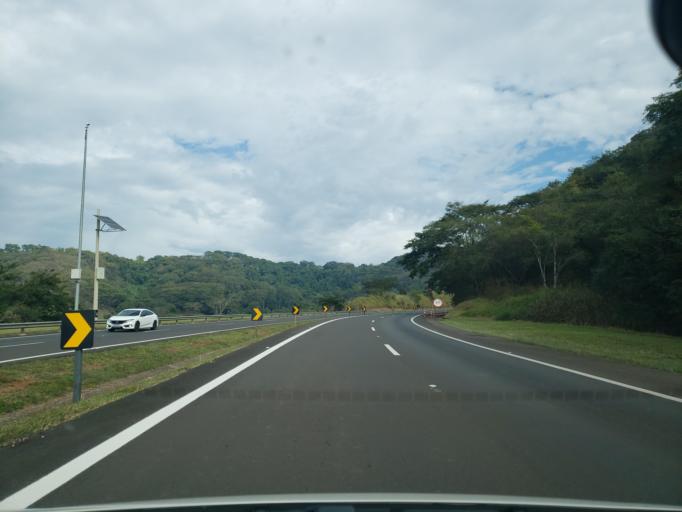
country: BR
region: Sao Paulo
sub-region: Dois Corregos
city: Dois Corregos
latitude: -22.2495
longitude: -48.3372
